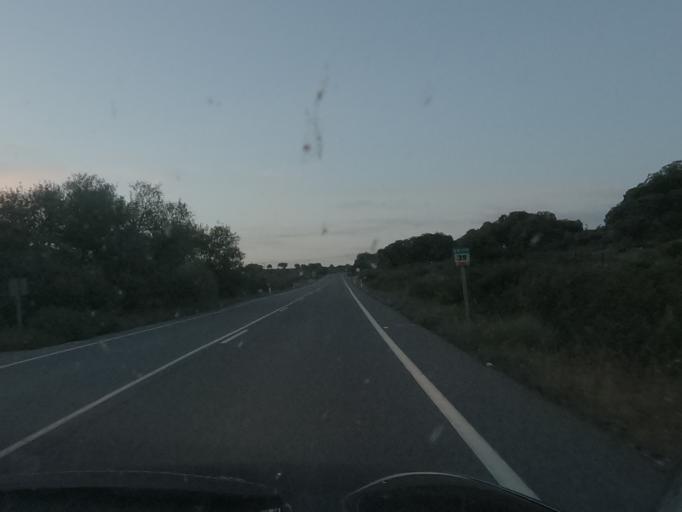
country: ES
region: Extremadura
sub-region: Provincia de Caceres
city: Alcantara
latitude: 39.7470
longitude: -6.9027
